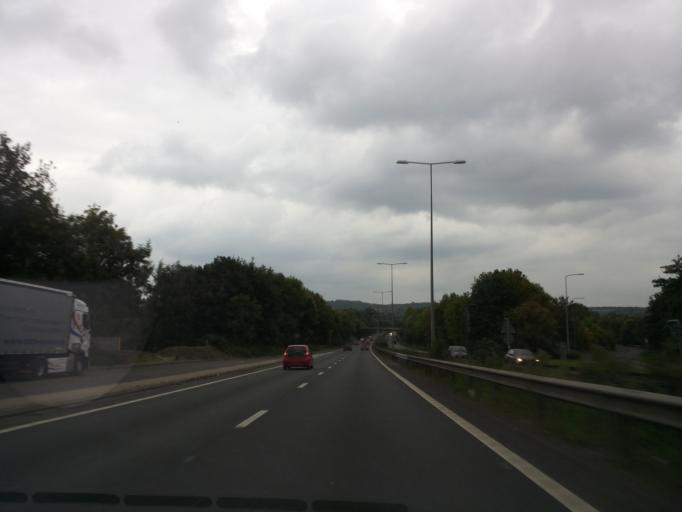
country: GB
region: England
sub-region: Kent
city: Dunkirk
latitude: 51.2991
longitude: 0.9364
